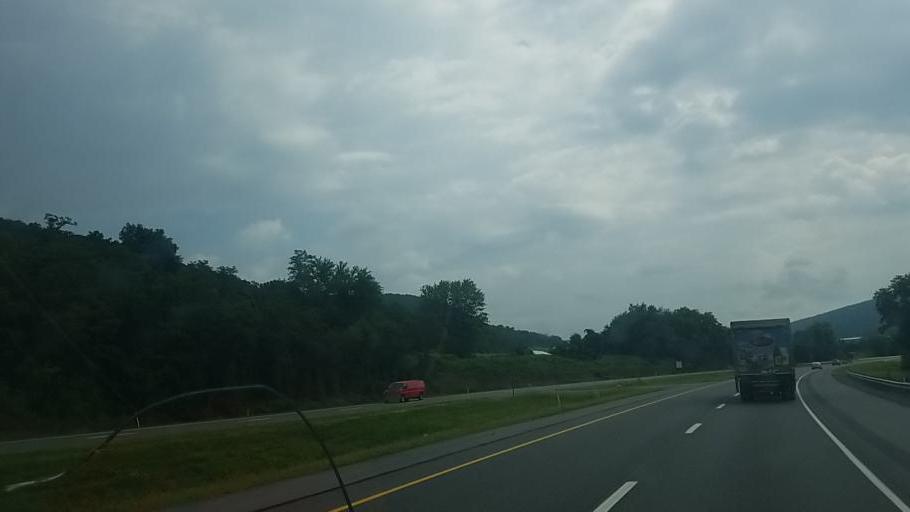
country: US
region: Pennsylvania
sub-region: Perry County
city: Newport
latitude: 40.5711
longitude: -77.2121
